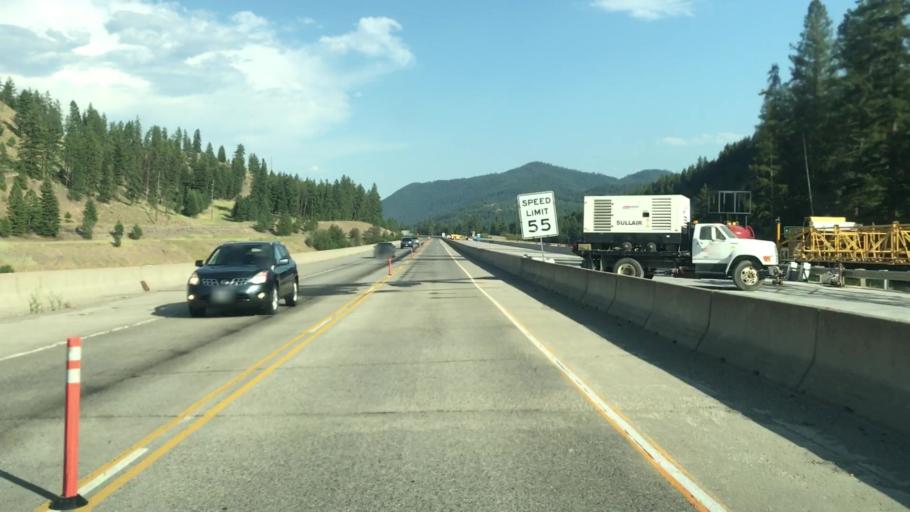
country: US
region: Montana
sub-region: Mineral County
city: Superior
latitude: 47.2219
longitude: -114.9628
